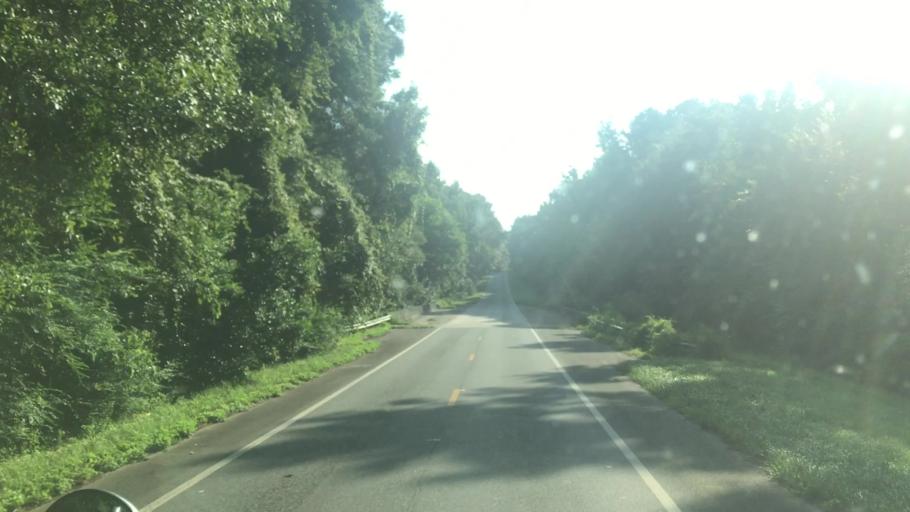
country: US
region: Florida
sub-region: Gadsden County
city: Quincy
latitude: 30.6682
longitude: -84.5501
